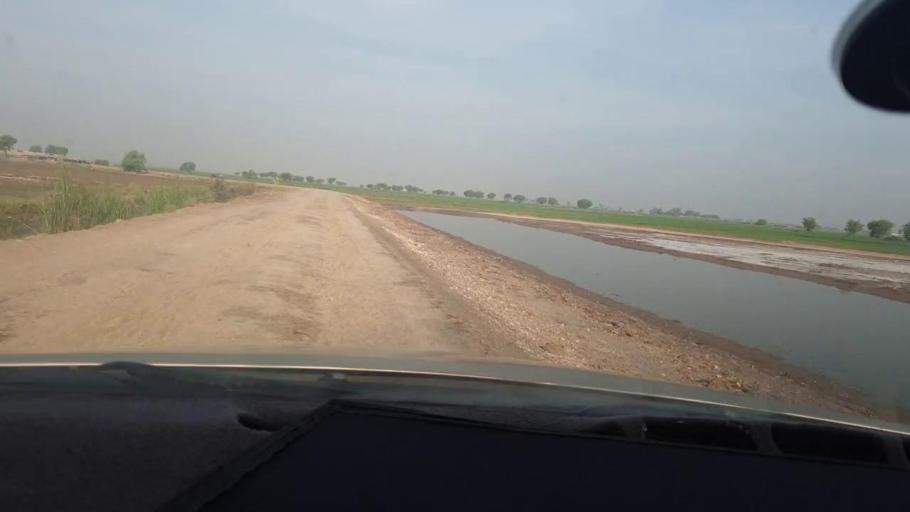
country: PK
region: Sindh
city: Jacobabad
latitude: 28.3360
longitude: 68.4077
